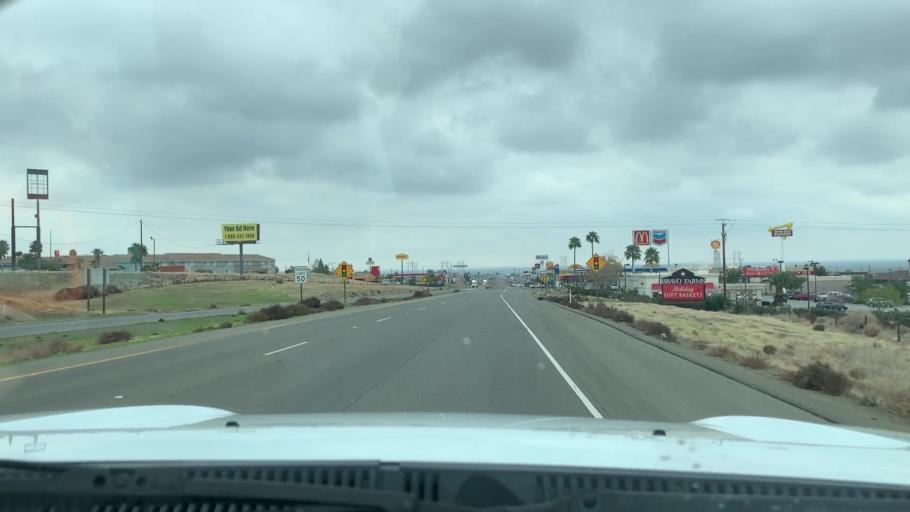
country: US
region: California
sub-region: Kings County
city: Kettleman City
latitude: 35.9848
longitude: -119.9596
